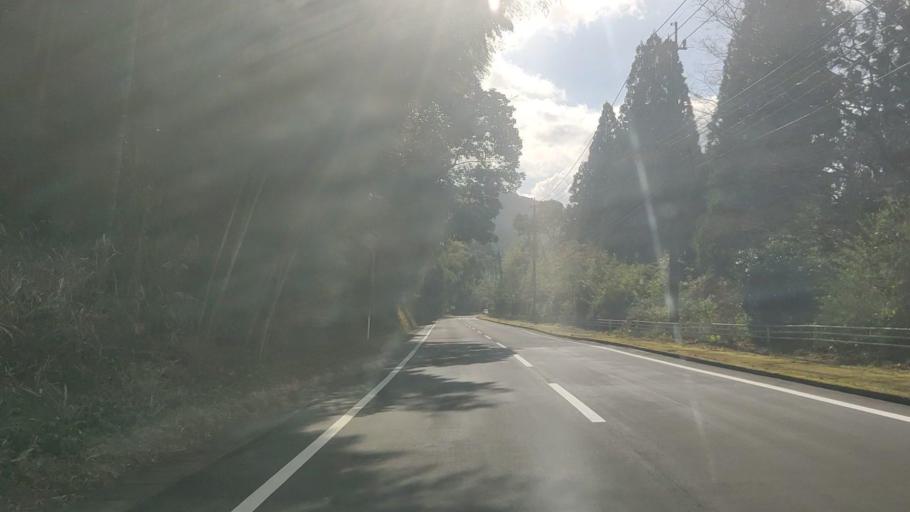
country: JP
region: Kagoshima
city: Okuchi-shinohara
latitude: 31.9846
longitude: 130.7428
